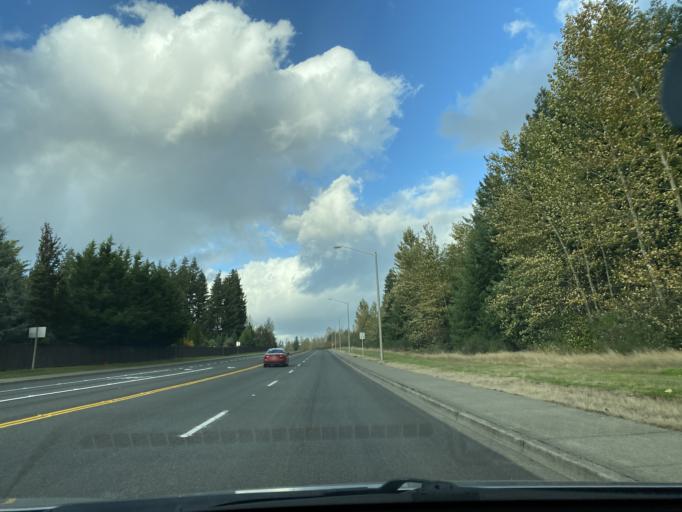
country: US
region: Washington
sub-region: Pierce County
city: Graham
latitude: 47.0914
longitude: -122.2680
